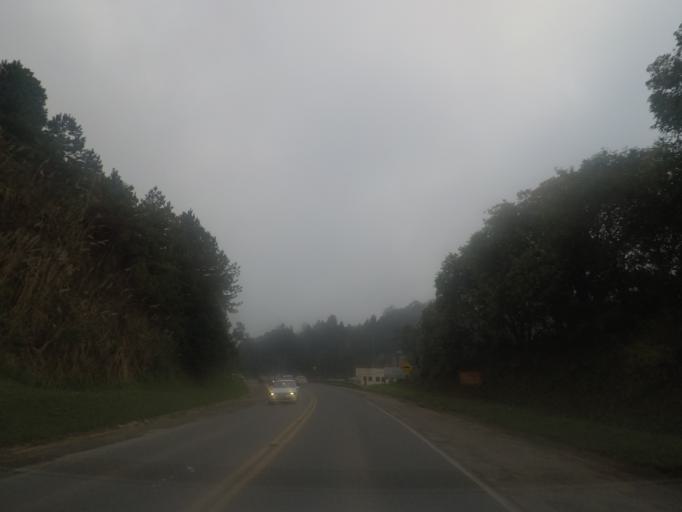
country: BR
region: Parana
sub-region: Almirante Tamandare
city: Almirante Tamandare
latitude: -25.3086
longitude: -49.3036
